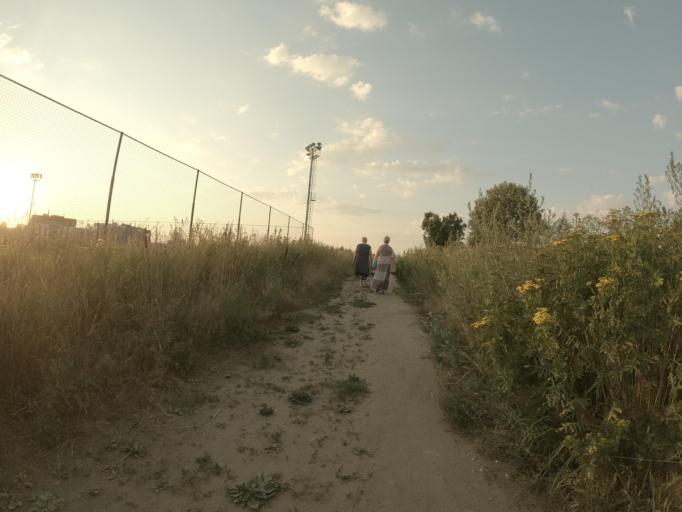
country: RU
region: Leningrad
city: Kirovsk
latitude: 59.8485
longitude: 30.9444
